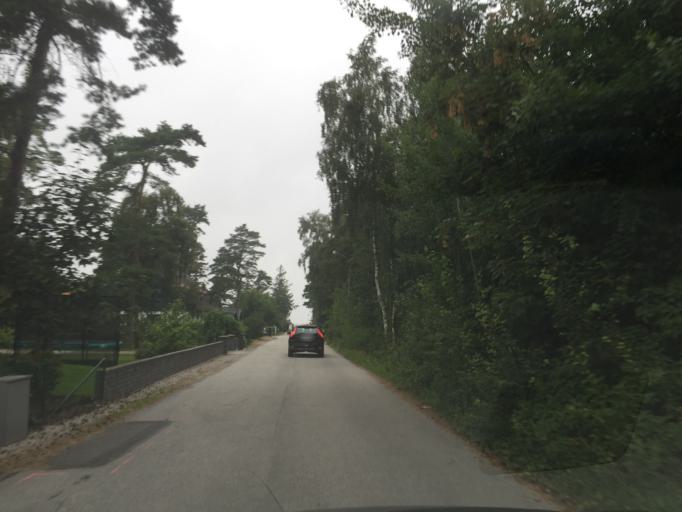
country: SE
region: Skane
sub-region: Vellinge Kommun
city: Hollviken
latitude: 55.4108
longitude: 12.9421
